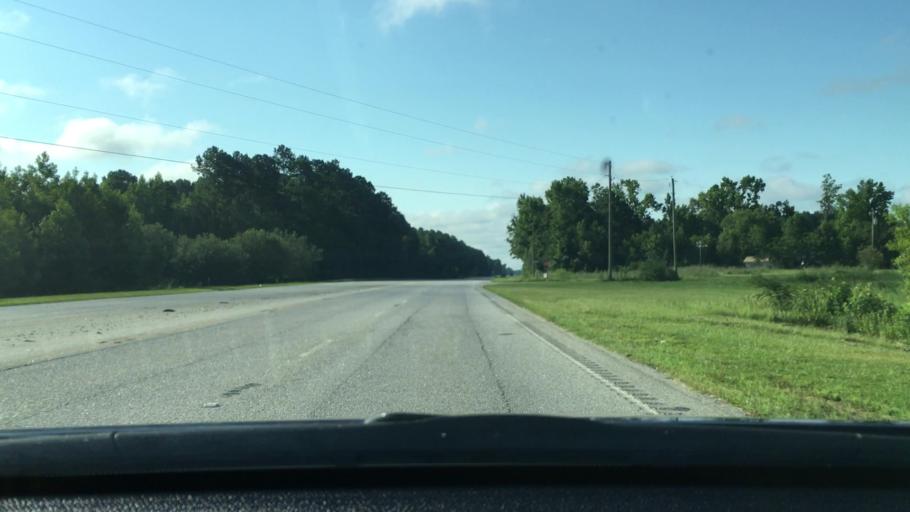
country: US
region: South Carolina
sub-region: Clarendon County
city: Manning
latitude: 33.7759
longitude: -80.2407
